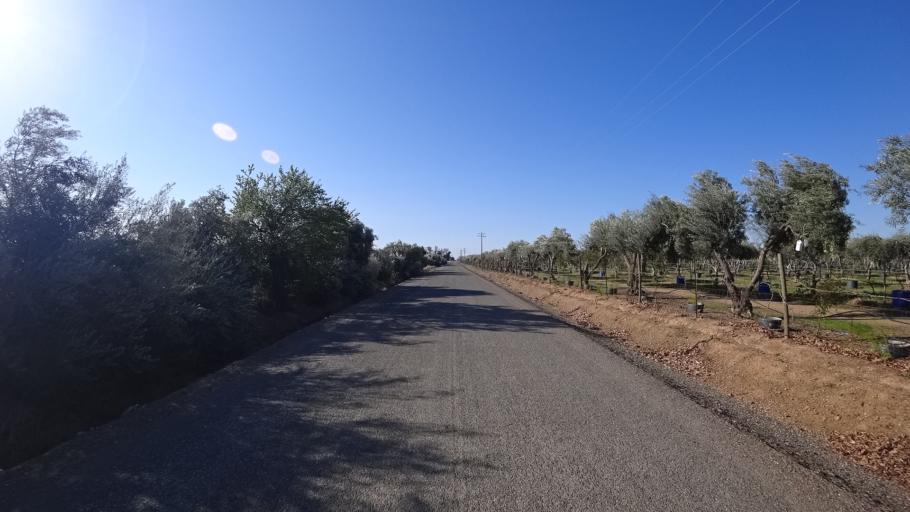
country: US
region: California
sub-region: Glenn County
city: Orland
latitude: 39.7719
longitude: -122.1227
